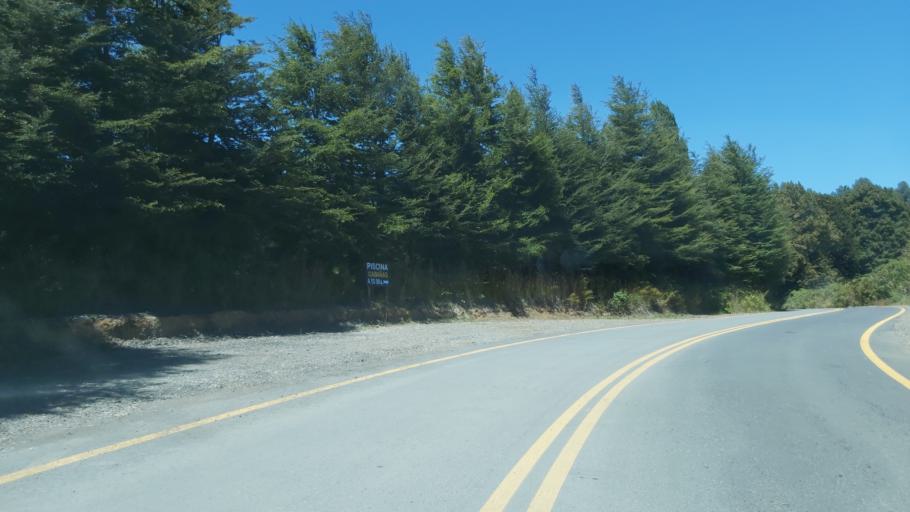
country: CL
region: Araucania
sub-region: Provincia de Cautin
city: Vilcun
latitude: -38.4651
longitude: -71.7631
